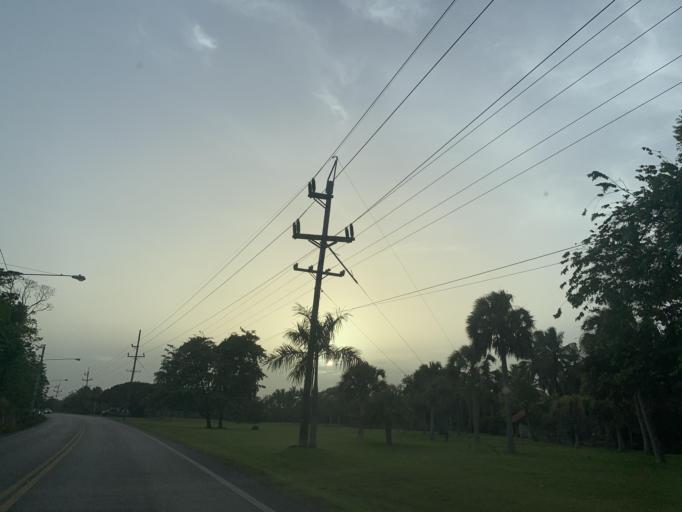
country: DO
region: Puerto Plata
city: Cabarete
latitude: 19.7788
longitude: -70.4804
